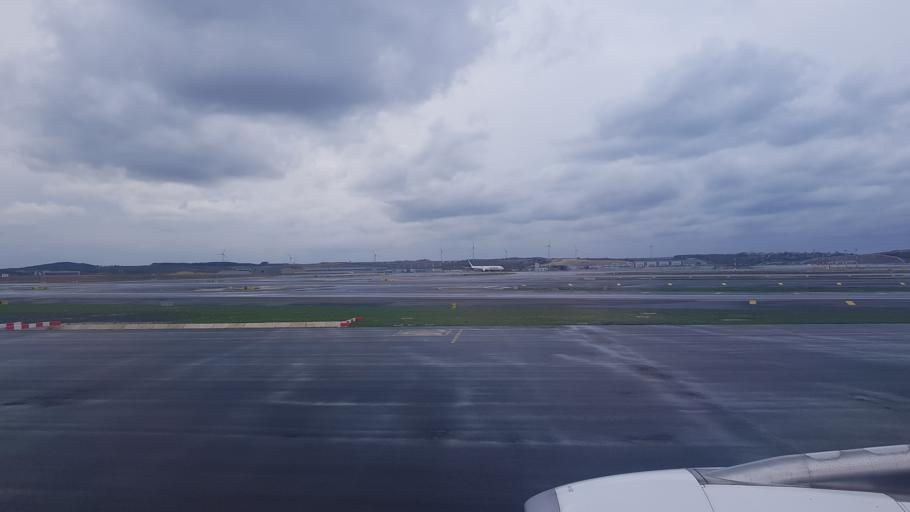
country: TR
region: Istanbul
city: Durusu
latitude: 41.2649
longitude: 28.7341
